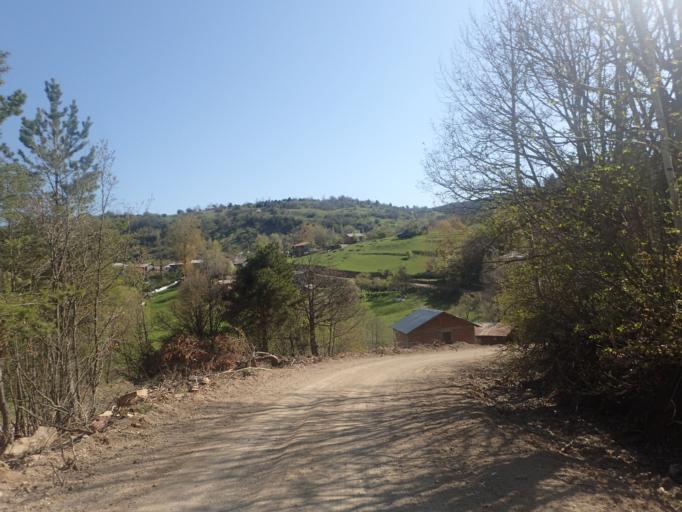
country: TR
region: Ordu
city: Mesudiye
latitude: 40.4169
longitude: 37.8354
